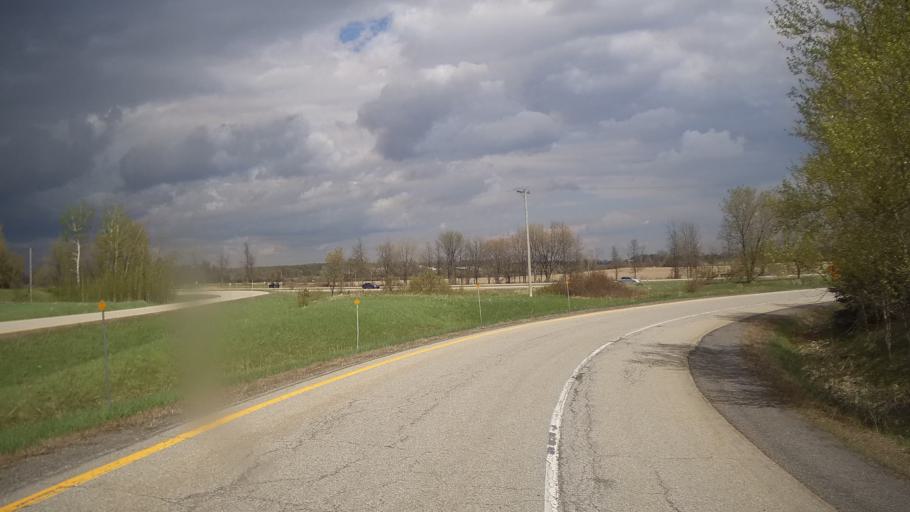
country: CA
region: Ontario
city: Hawkesbury
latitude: 45.5186
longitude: -74.5658
